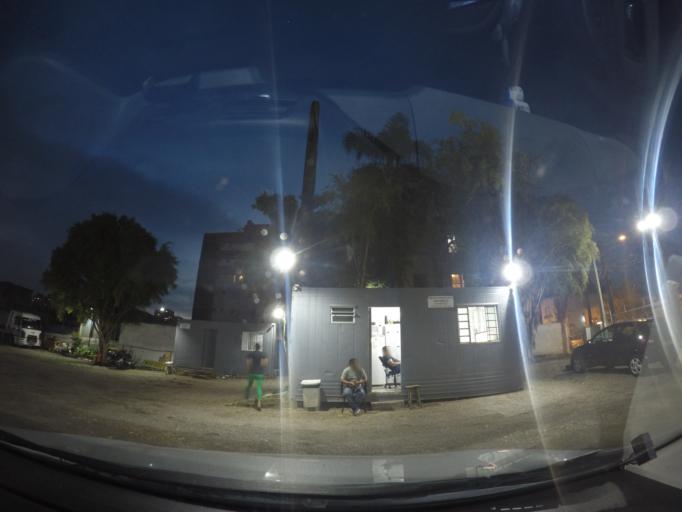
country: BR
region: Parana
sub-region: Curitiba
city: Curitiba
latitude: -25.4262
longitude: -49.2835
